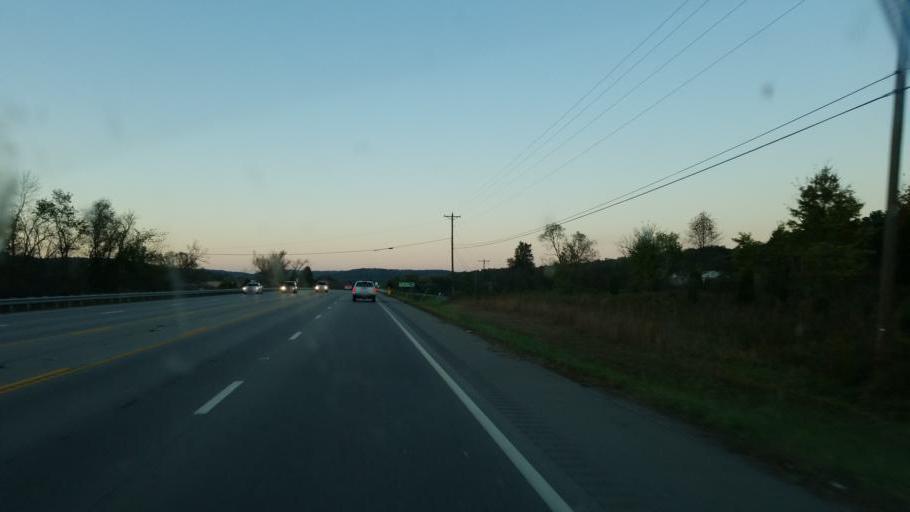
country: US
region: Ohio
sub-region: Pike County
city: Waverly
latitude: 39.1621
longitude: -82.9762
